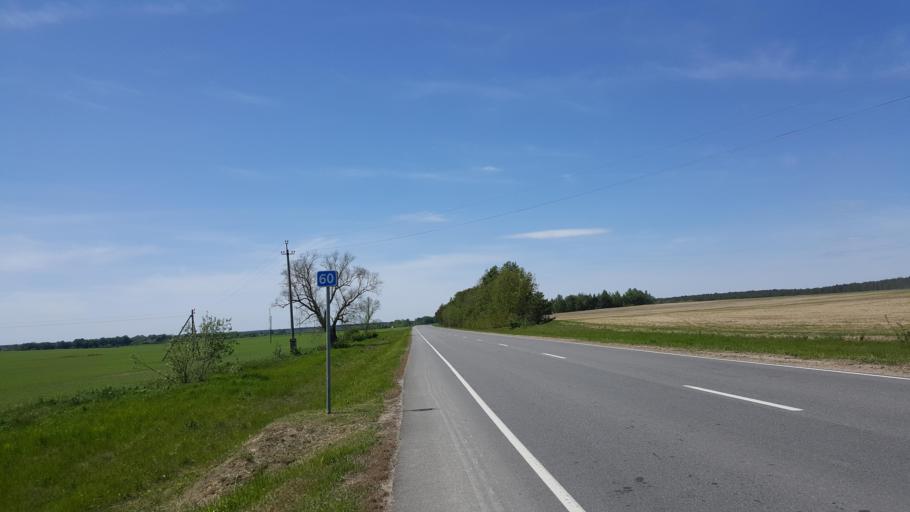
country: BY
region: Brest
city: Kobryn
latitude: 52.3543
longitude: 24.1813
